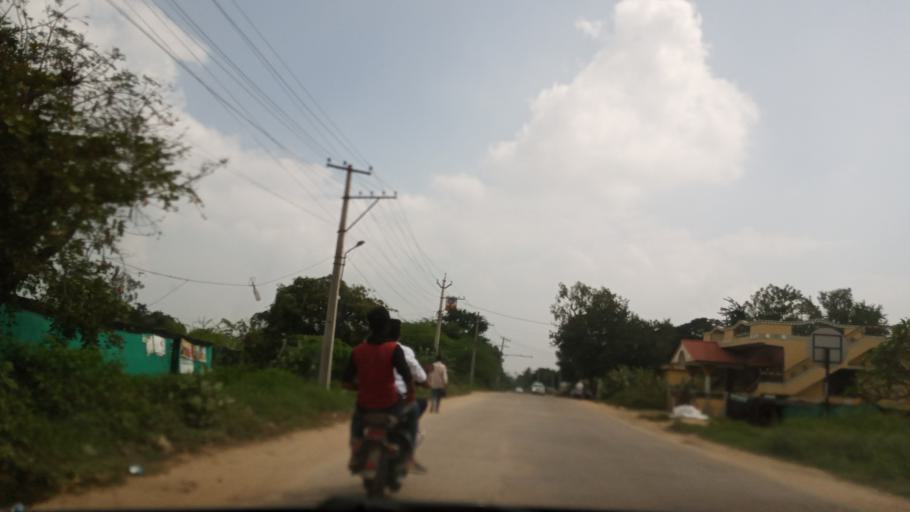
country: IN
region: Andhra Pradesh
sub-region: Chittoor
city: Madanapalle
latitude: 13.6384
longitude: 78.6355
